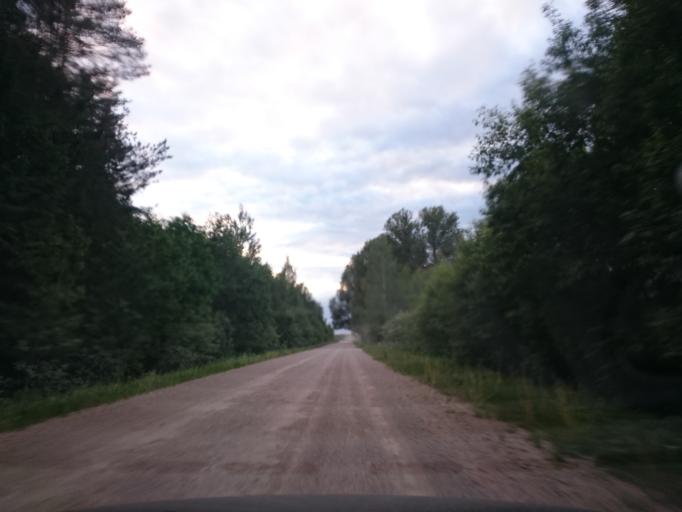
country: LV
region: Ropazu
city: Ropazi
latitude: 56.9568
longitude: 24.7160
